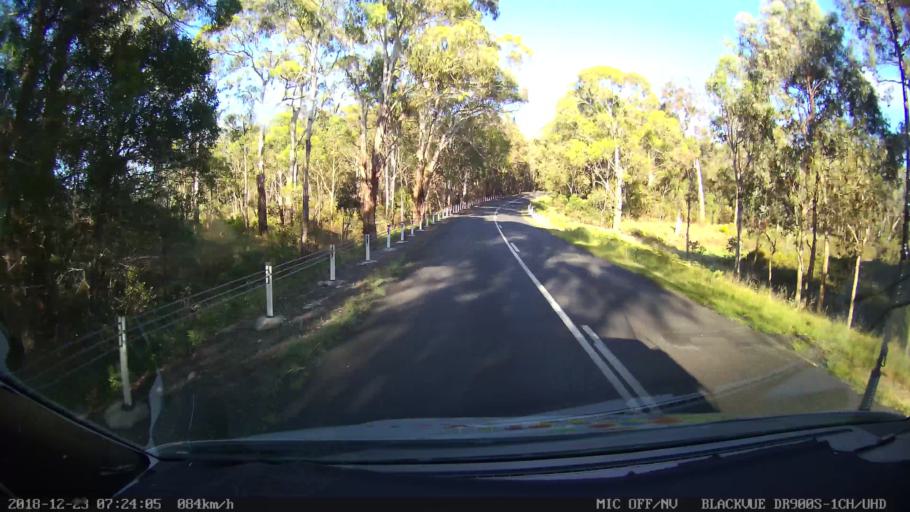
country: AU
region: New South Wales
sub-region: Armidale Dumaresq
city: Enmore
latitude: -30.5044
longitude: 152.2274
